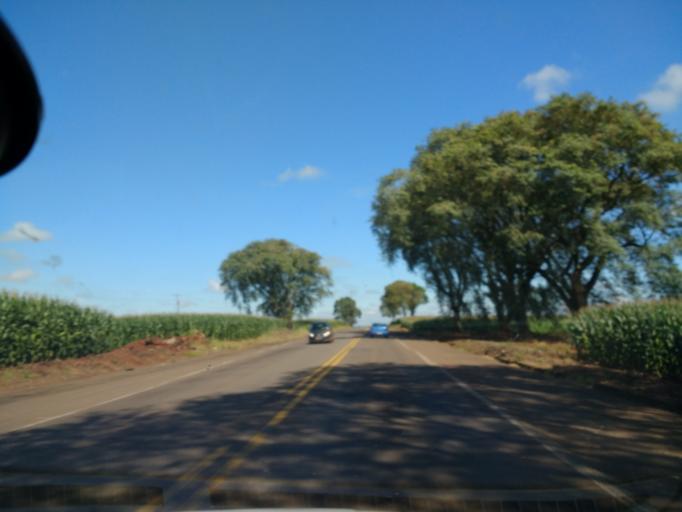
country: BR
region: Parana
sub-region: Terra Boa
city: Terra Boa
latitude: -23.6089
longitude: -52.4198
